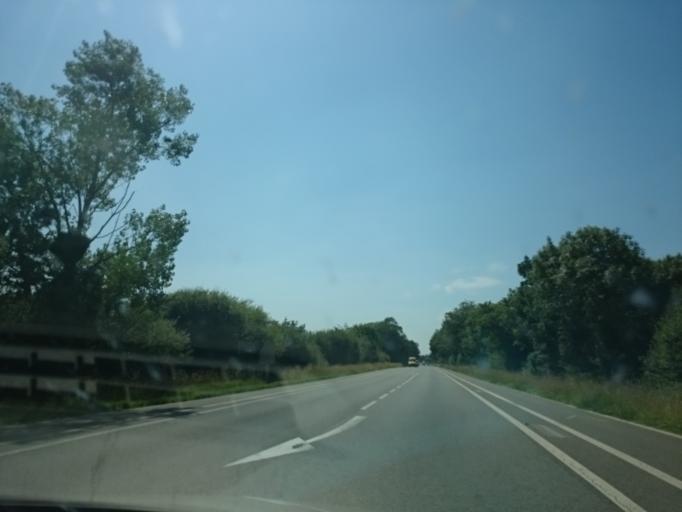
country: FR
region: Pays de la Loire
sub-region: Departement de la Loire-Atlantique
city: La Montagne
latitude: 47.2089
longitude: -1.6908
